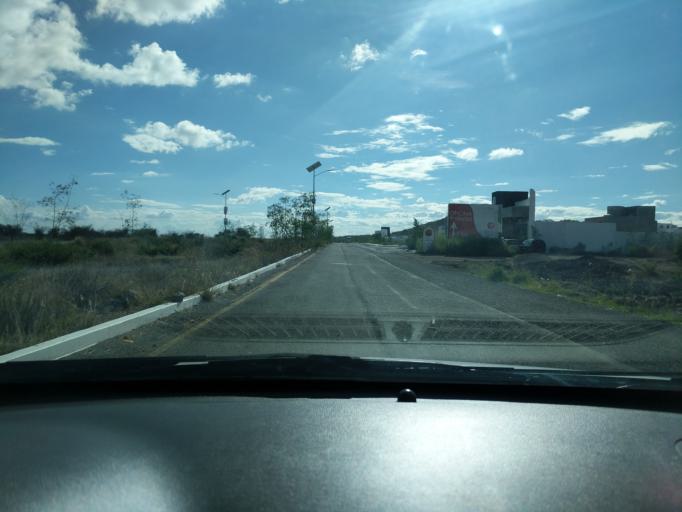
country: MX
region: Queretaro
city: La Canada
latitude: 20.5970
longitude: -100.3065
